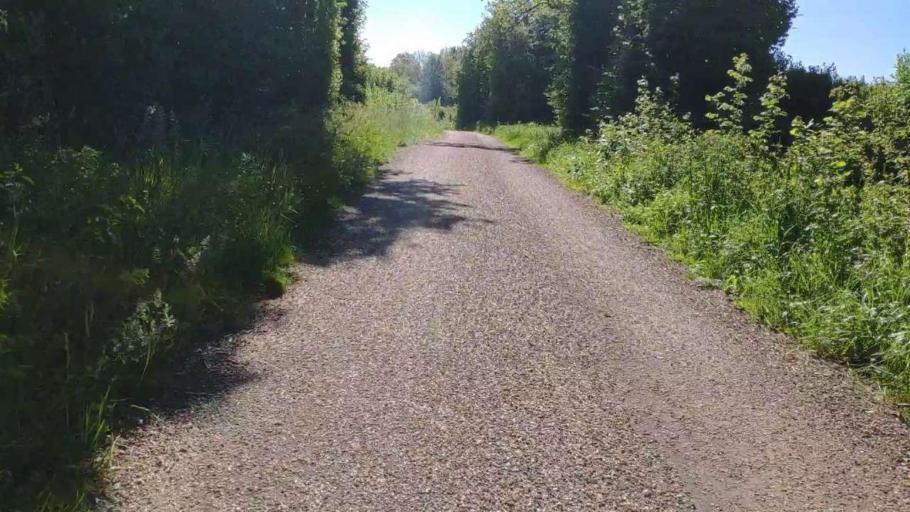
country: FR
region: Franche-Comte
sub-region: Departement du Jura
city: Perrigny
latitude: 46.6857
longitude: 5.6696
